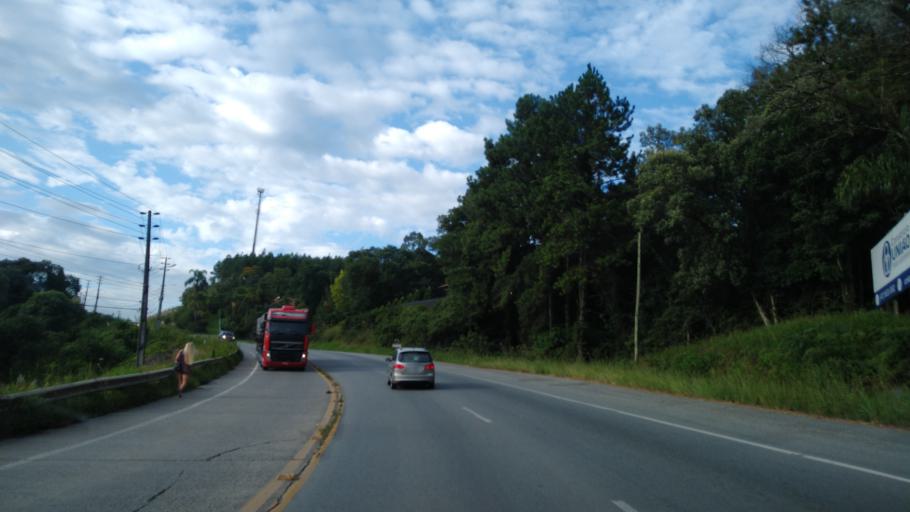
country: BR
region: Santa Catarina
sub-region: Sao Bento Do Sul
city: Sao Bento do Sul
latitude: -26.2310
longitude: -49.4264
